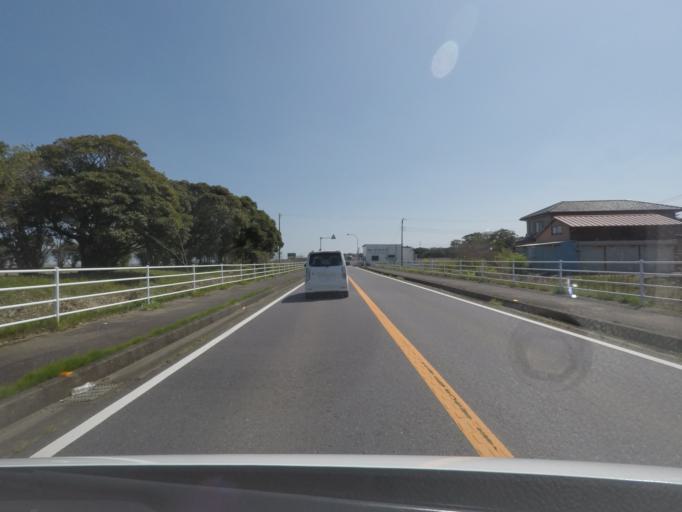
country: JP
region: Chiba
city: Asahi
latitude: 35.7975
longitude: 140.7205
